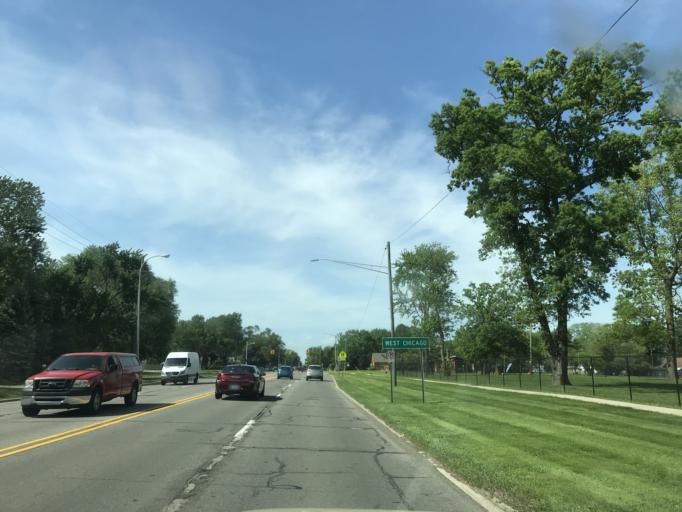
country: US
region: Michigan
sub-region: Wayne County
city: Redford
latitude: 42.3609
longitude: -83.3130
